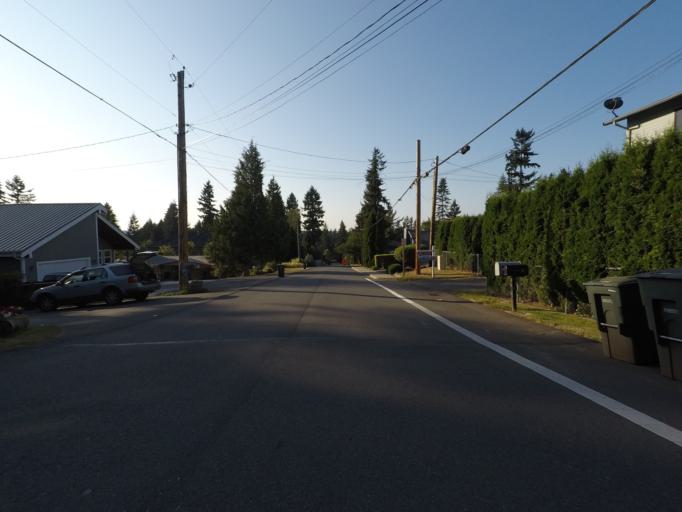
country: US
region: Washington
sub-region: King County
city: Kenmore
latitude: 47.7449
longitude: -122.2337
